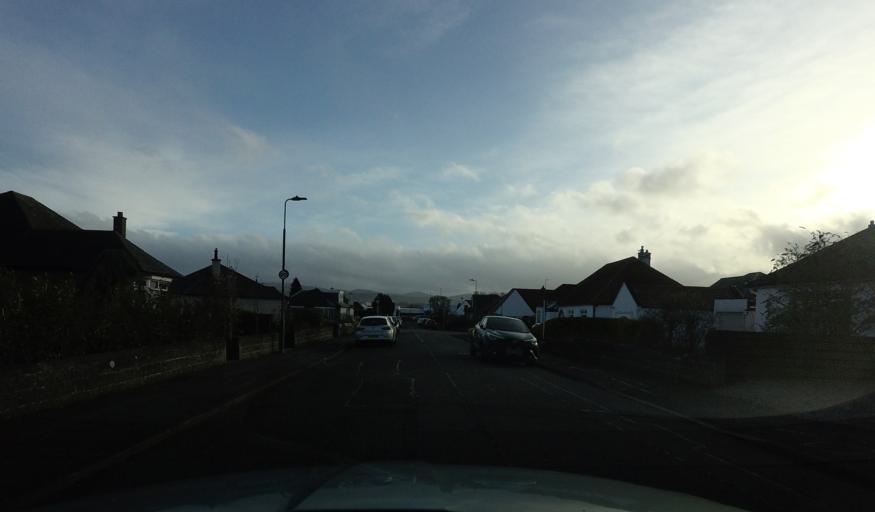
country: GB
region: Scotland
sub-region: Edinburgh
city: Currie
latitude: 55.9424
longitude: -3.3070
